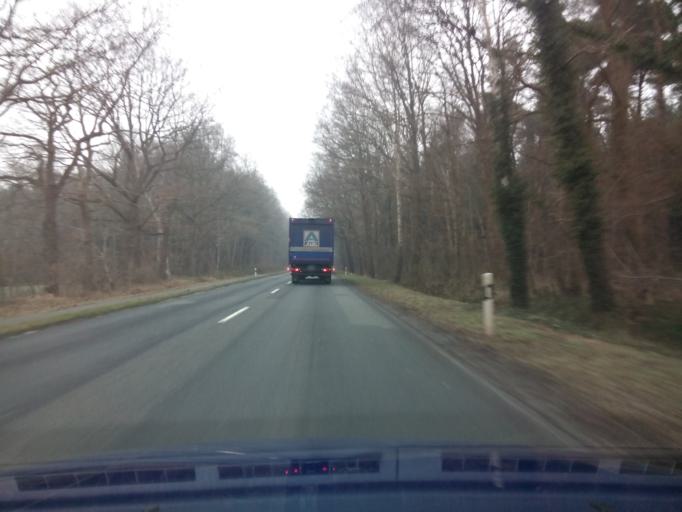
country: DE
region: Lower Saxony
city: Bramstedt
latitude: 53.3477
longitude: 8.6803
